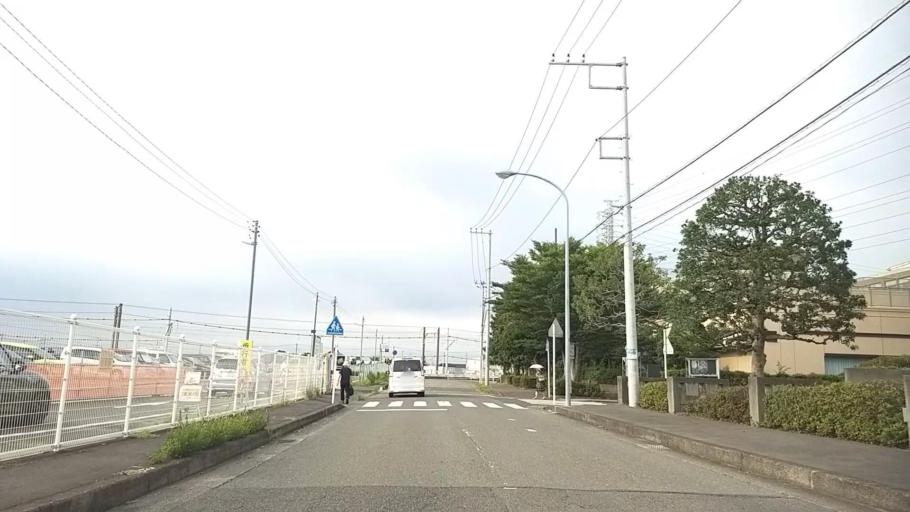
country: JP
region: Kanagawa
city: Atsugi
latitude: 35.4513
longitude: 139.3856
